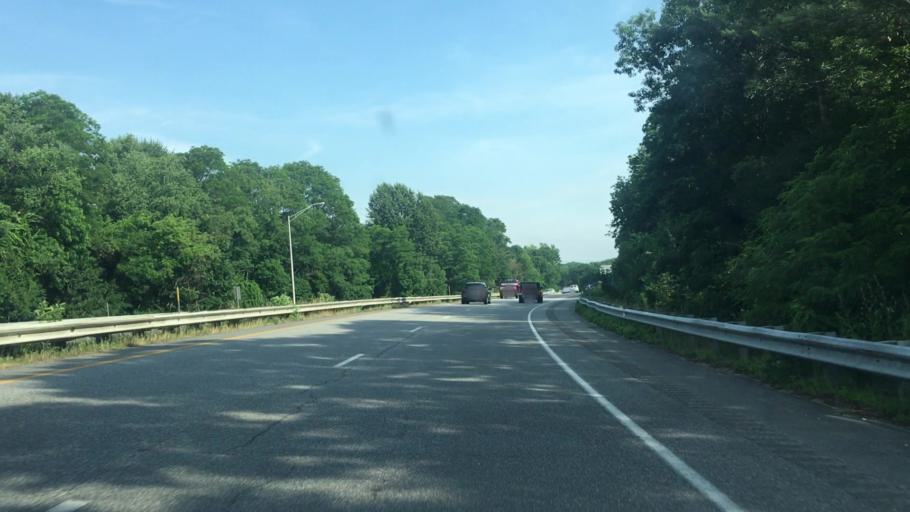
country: US
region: New Hampshire
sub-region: Strafford County
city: Dover
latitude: 43.1802
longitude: -70.8740
